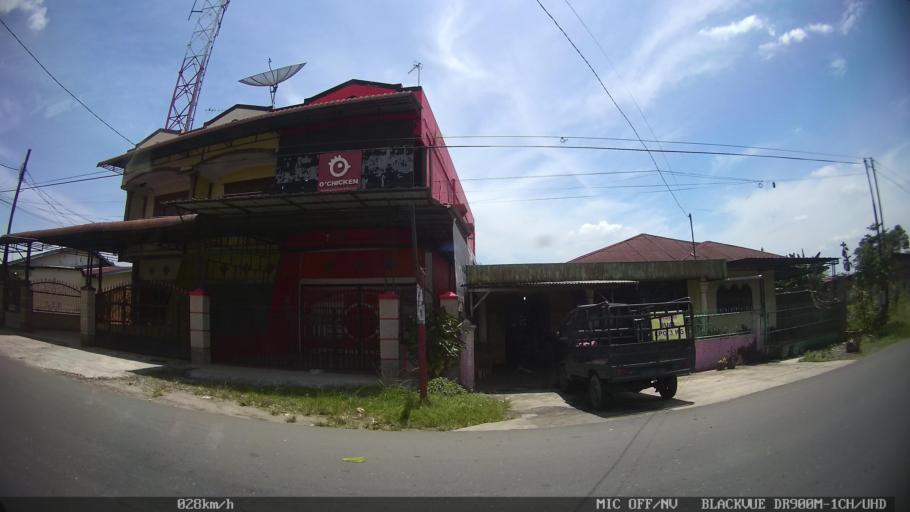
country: ID
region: North Sumatra
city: Binjai
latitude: 3.6018
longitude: 98.4963
